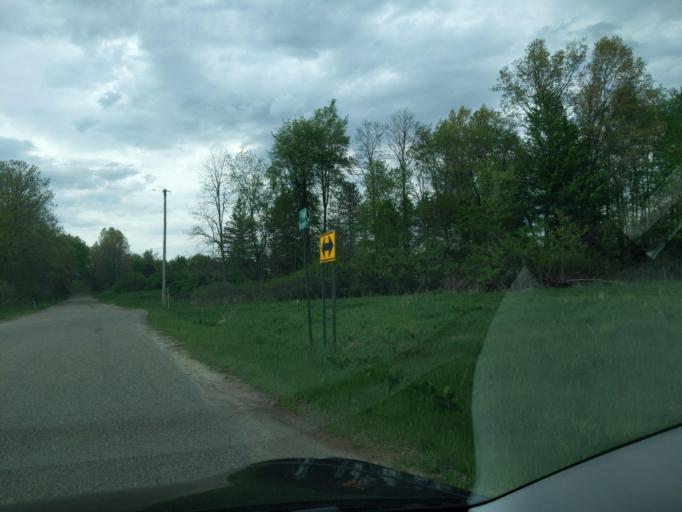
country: US
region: Michigan
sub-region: Ingham County
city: Stockbridge
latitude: 42.4382
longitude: -84.1407
